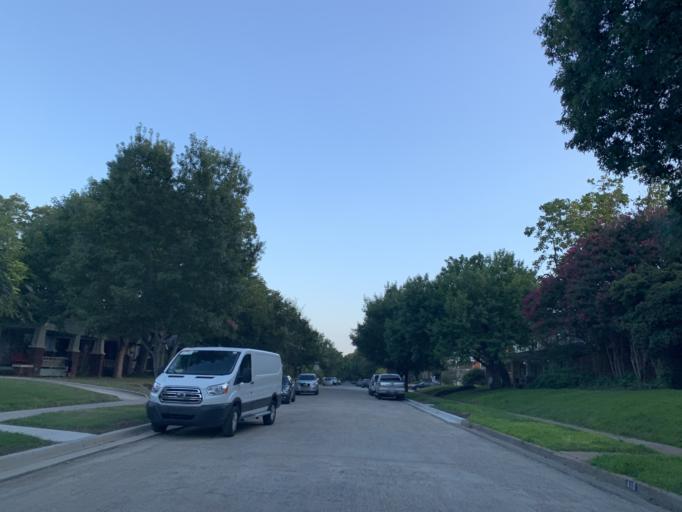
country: US
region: Texas
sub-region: Dallas County
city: Cockrell Hill
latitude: 32.7489
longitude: -96.8453
